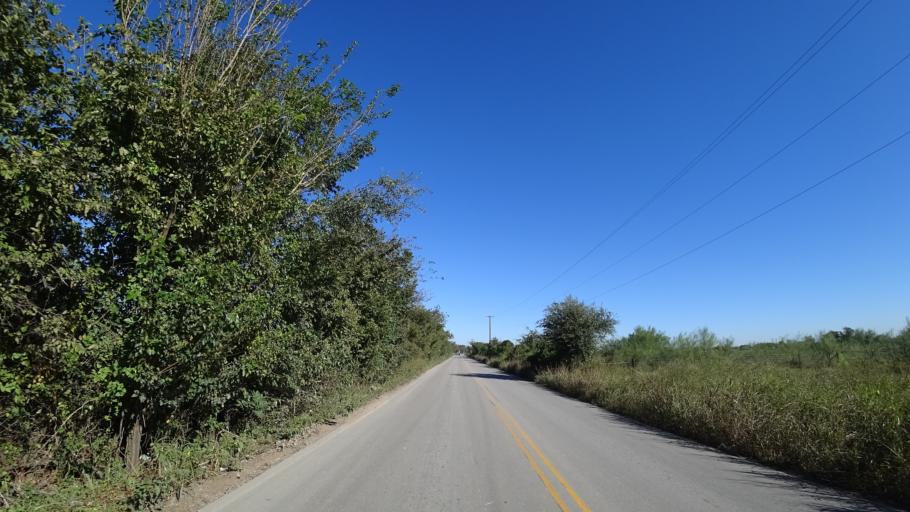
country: US
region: Texas
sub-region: Travis County
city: Austin
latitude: 30.2425
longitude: -97.6803
